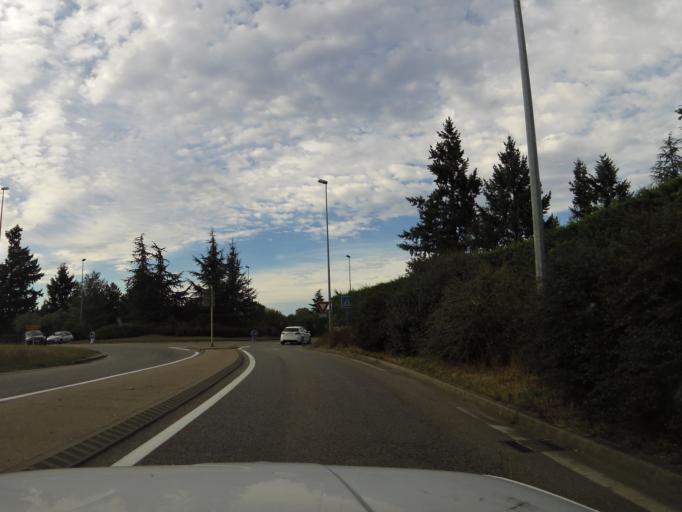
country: FR
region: Rhone-Alpes
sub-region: Departement de l'Ain
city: Saint-Jean-de-Niost
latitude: 45.8505
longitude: 5.2534
